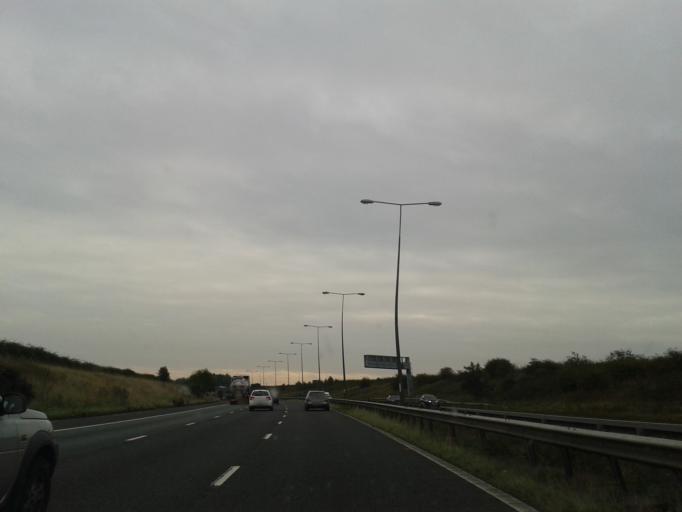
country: GB
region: England
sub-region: St. Helens
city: Billinge
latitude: 53.5161
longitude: -2.6929
